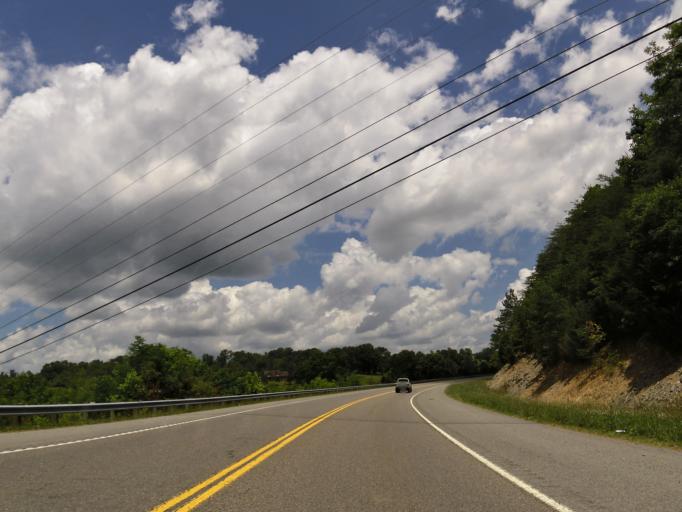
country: US
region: Tennessee
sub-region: Claiborne County
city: New Tazewell
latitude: 36.4131
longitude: -83.6595
